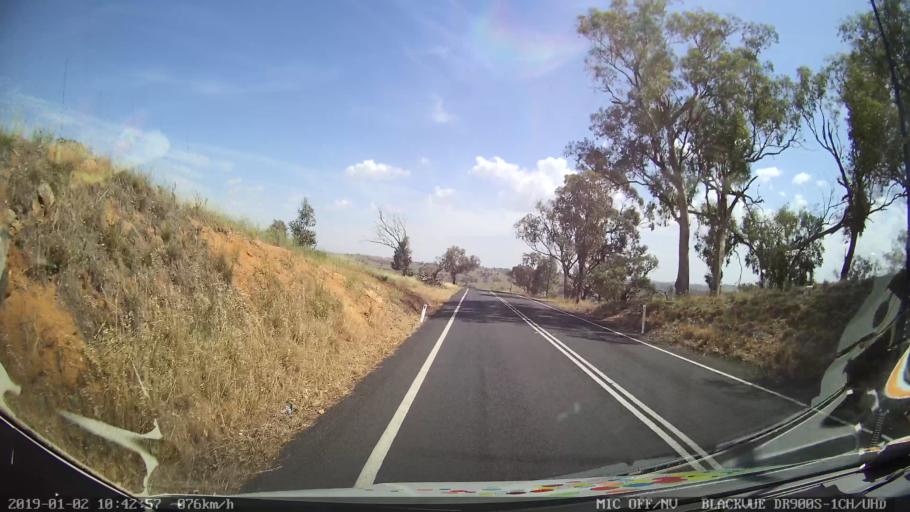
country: AU
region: New South Wales
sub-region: Cootamundra
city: Cootamundra
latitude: -34.7783
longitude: 148.3062
